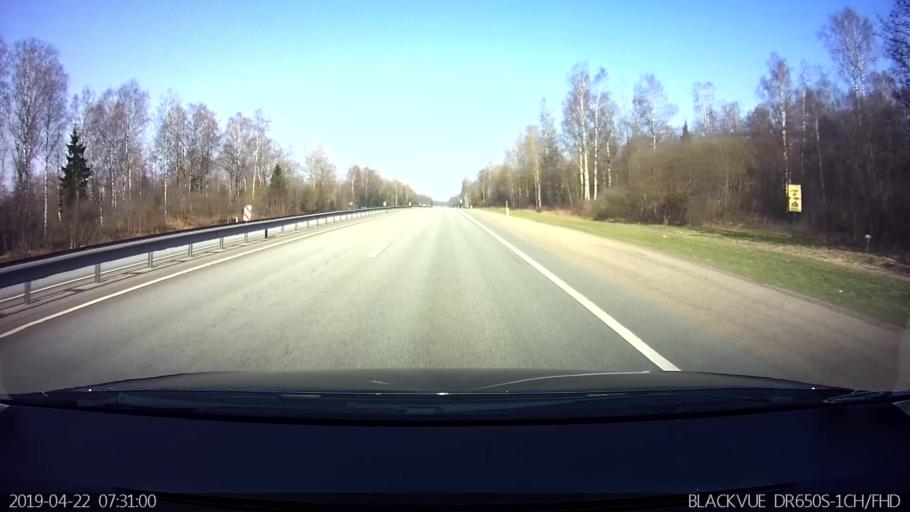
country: RU
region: Smolensk
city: Vyaz'ma
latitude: 55.1957
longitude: 33.9295
